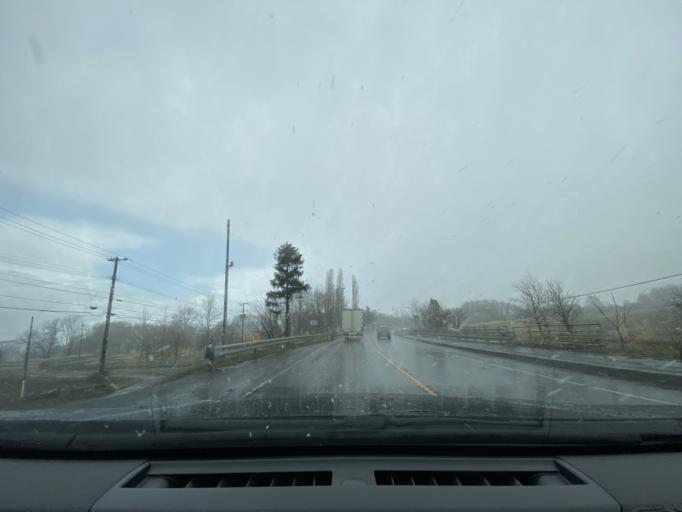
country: JP
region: Hokkaido
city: Takikawa
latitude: 43.6412
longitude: 141.9489
